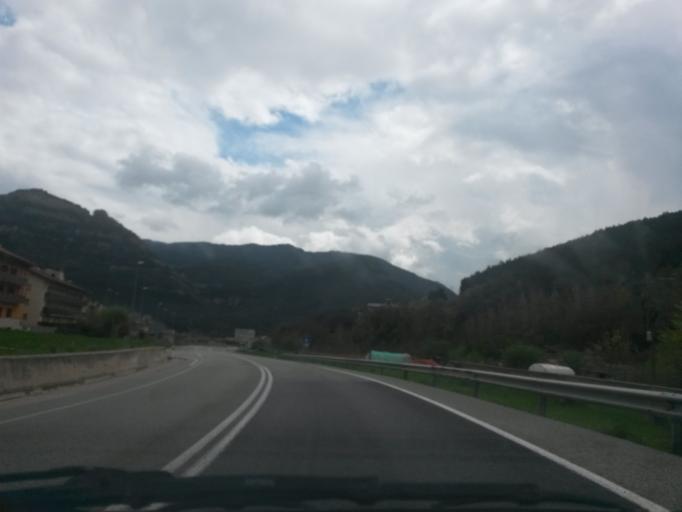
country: ES
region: Catalonia
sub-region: Provincia de Barcelona
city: Guardiola de Bergueda
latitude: 42.2399
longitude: 1.8738
